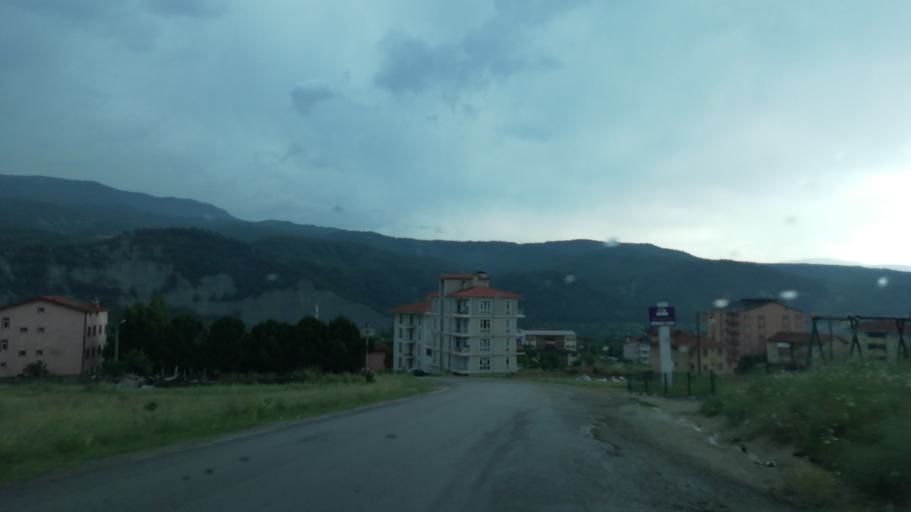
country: TR
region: Karabuk
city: Safranbolu
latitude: 41.2205
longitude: 32.6861
